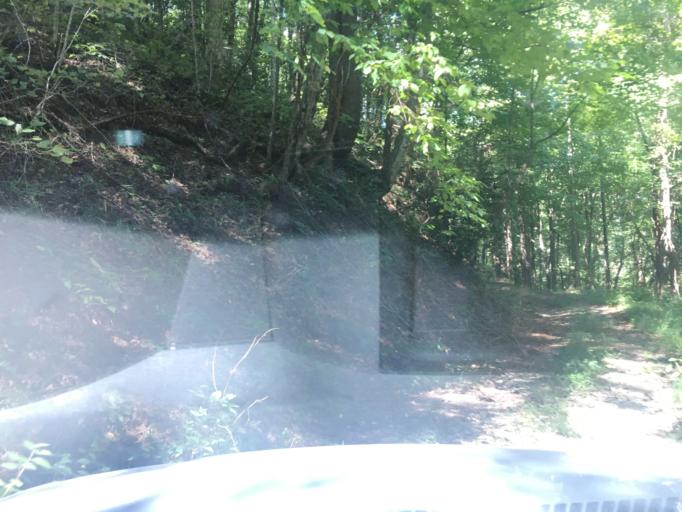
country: US
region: North Carolina
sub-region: Graham County
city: Robbinsville
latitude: 35.2682
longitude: -83.6808
